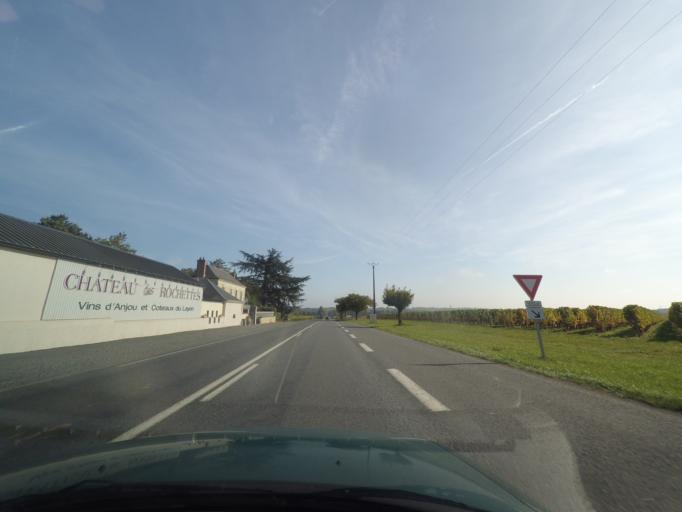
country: FR
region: Pays de la Loire
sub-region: Departement de Maine-et-Loire
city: Nueil-sur-Layon
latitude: 47.1707
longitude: -0.3573
